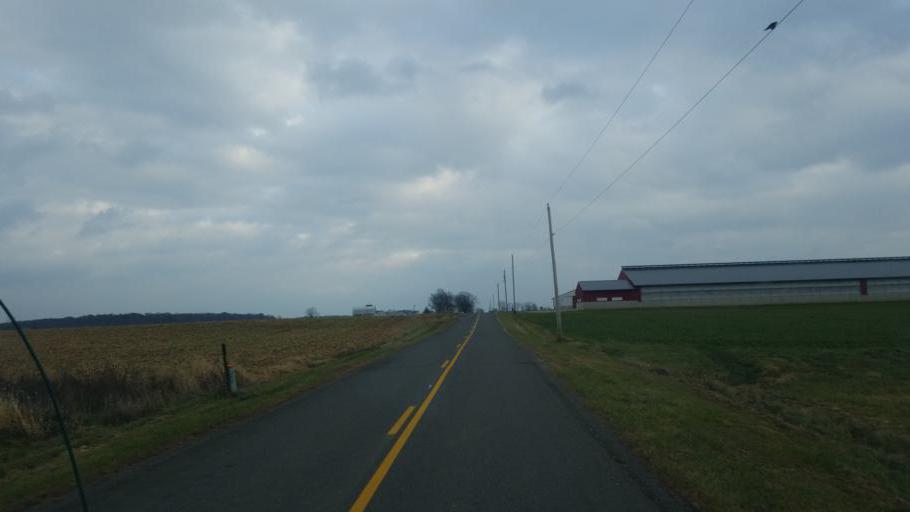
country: US
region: Ohio
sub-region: Mercer County
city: Coldwater
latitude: 40.5090
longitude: -84.7021
